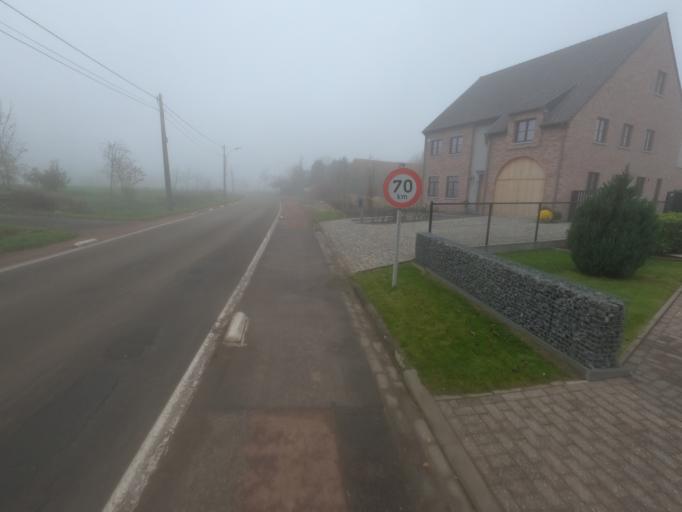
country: BE
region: Flanders
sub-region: Provincie Oost-Vlaanderen
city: Kruibeke
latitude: 51.1706
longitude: 4.2750
